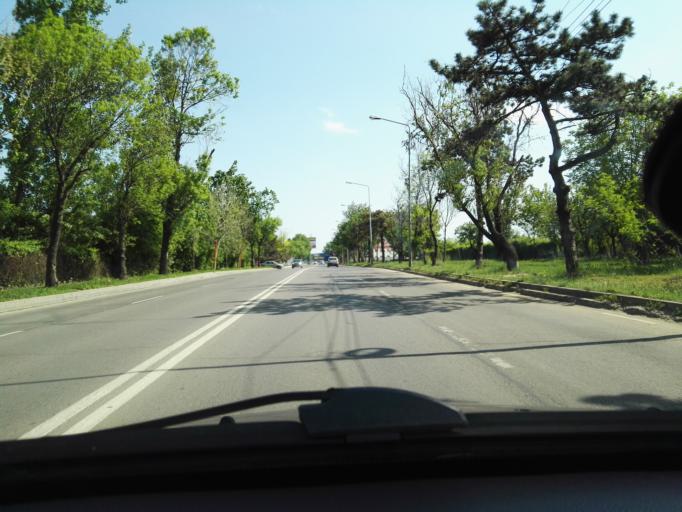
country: RO
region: Ilfov
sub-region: Comuna Popesti-Leordeni
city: Popesti-Leordeni
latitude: 44.3679
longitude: 26.1246
